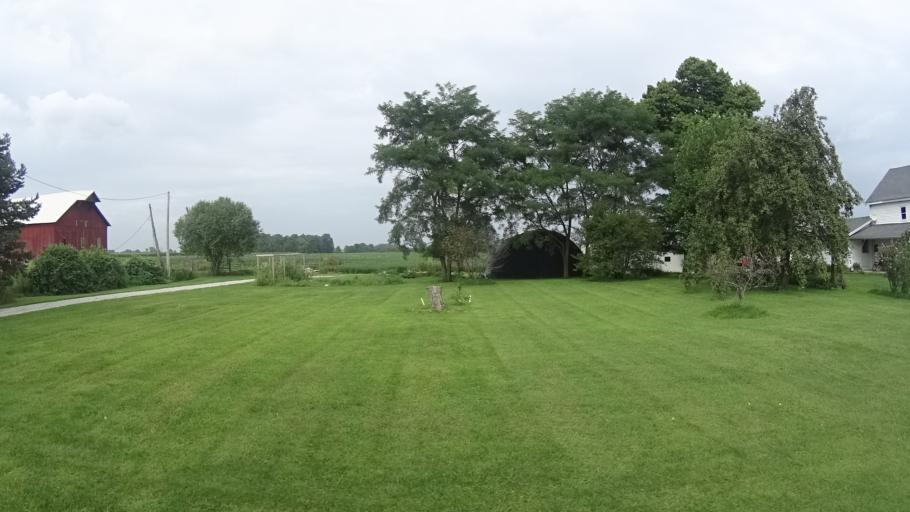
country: US
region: Indiana
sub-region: Madison County
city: Lapel
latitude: 40.0261
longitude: -85.8055
